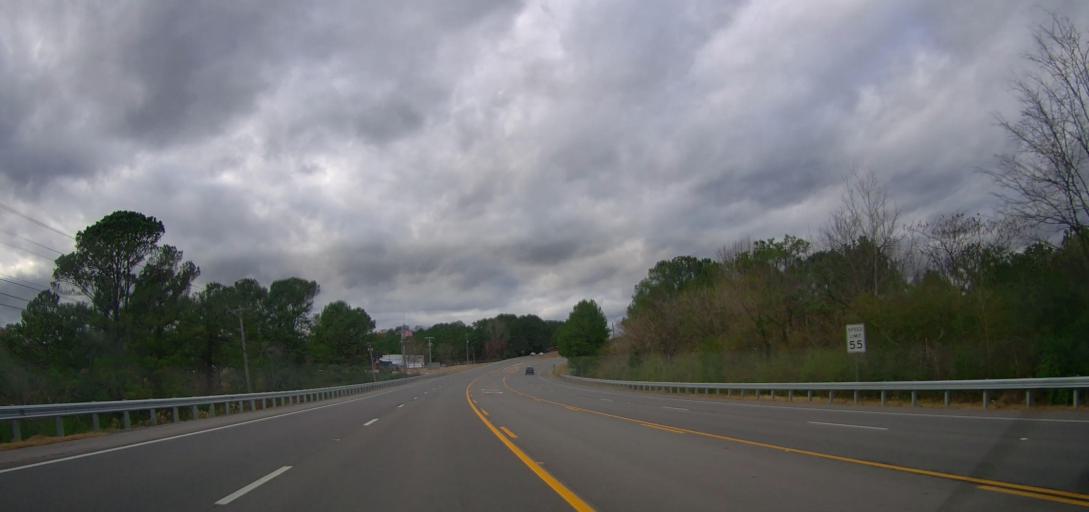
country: US
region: Alabama
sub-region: Cullman County
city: Cullman
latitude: 34.2088
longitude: -86.8849
